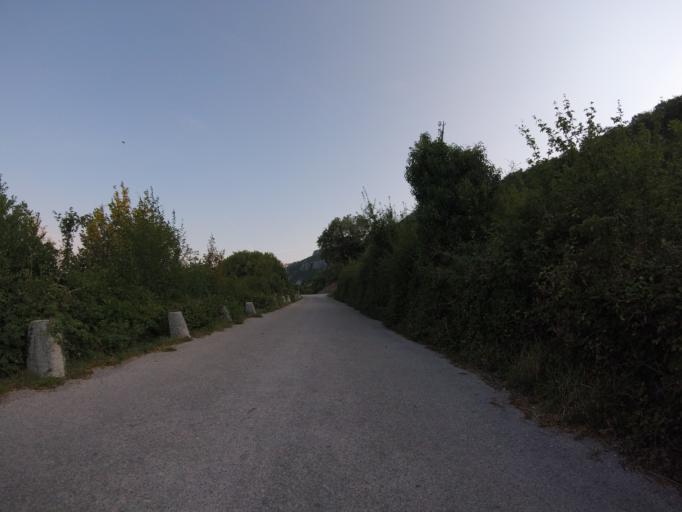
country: HR
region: Primorsko-Goranska
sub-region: Grad Crikvenica
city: Crikvenica
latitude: 45.1948
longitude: 14.7223
